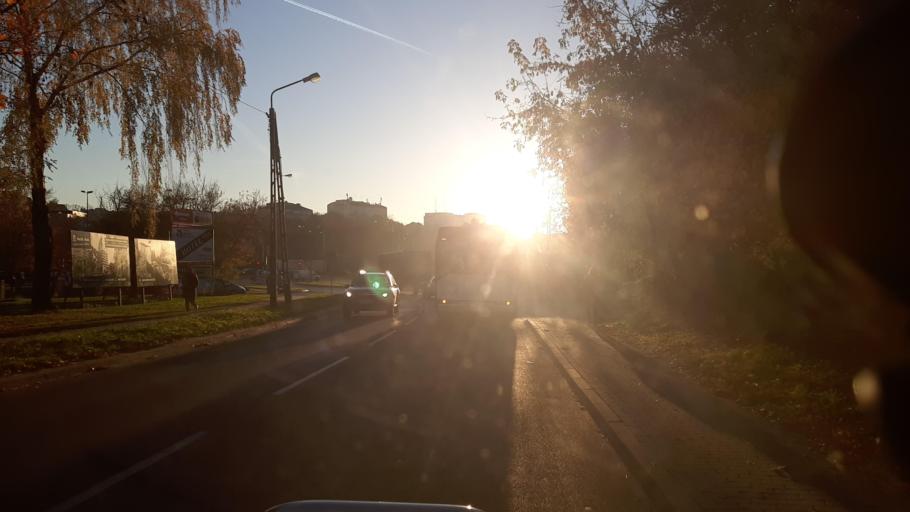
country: PL
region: Lublin Voivodeship
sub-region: Powiat lubelski
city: Lublin
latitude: 51.2542
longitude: 22.5621
